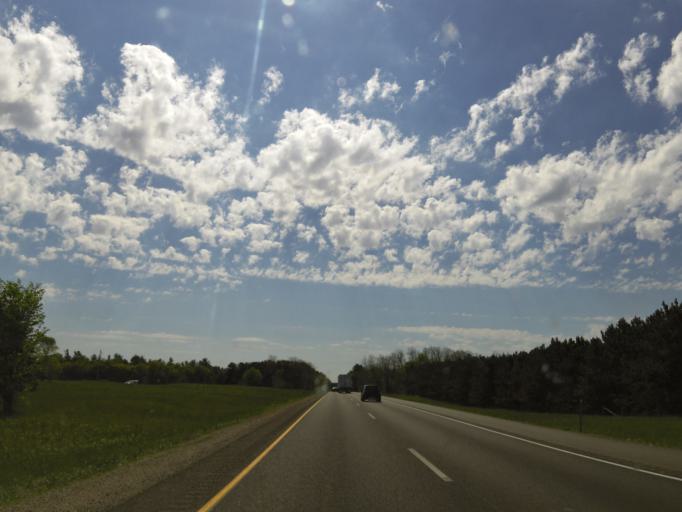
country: US
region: Wisconsin
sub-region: Eau Claire County
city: Altoona
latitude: 44.7536
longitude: -91.3913
